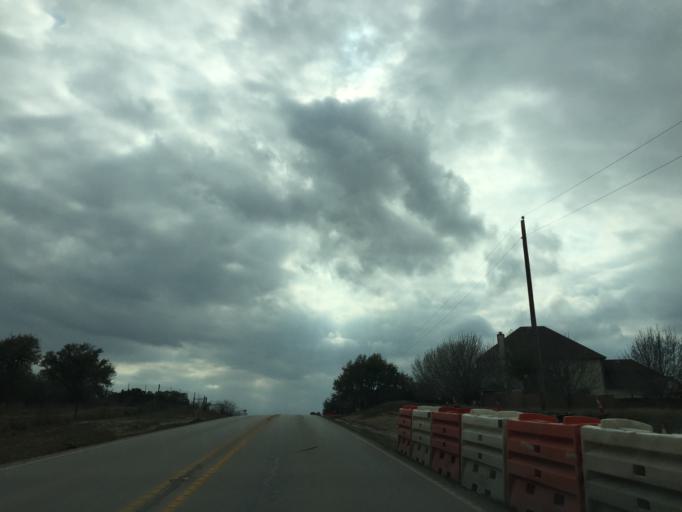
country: US
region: Texas
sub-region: Travis County
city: Shady Hollow
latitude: 30.1565
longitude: -97.9666
